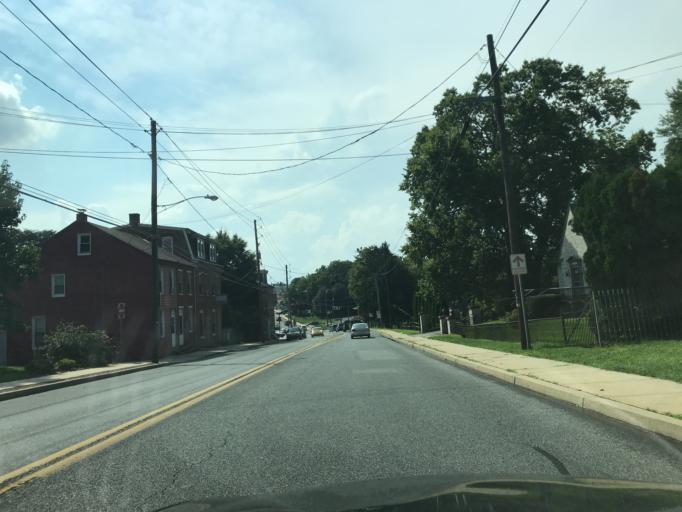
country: US
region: Pennsylvania
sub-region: Lancaster County
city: Columbia
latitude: 40.0316
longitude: -76.4883
